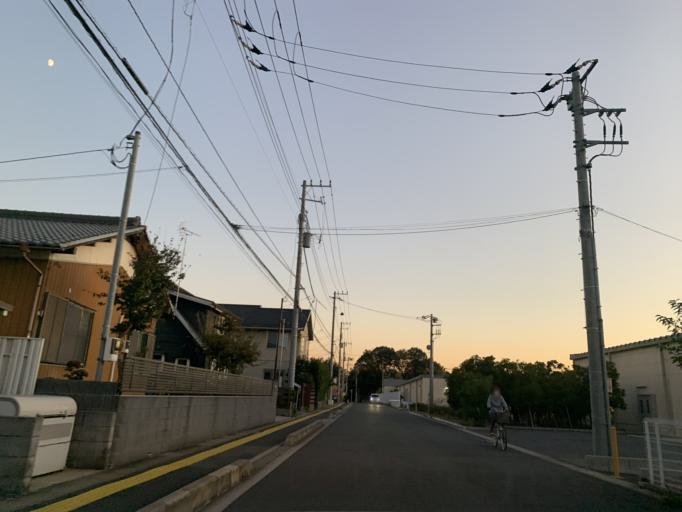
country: JP
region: Chiba
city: Nagareyama
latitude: 35.9001
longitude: 139.9311
